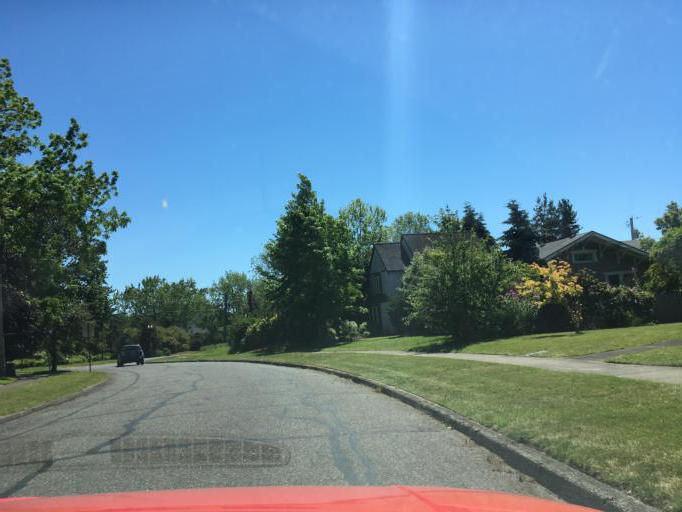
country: US
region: Washington
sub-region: Whatcom County
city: Bellingham
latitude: 48.7665
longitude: -122.4800
